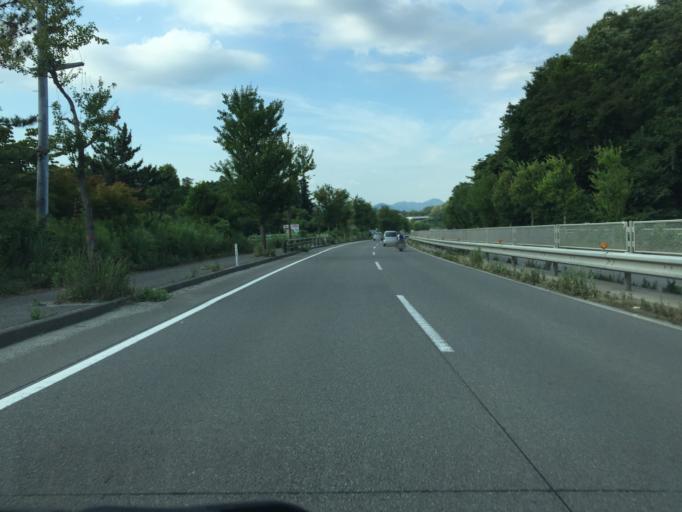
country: JP
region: Fukushima
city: Nihommatsu
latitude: 37.6206
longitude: 140.4749
